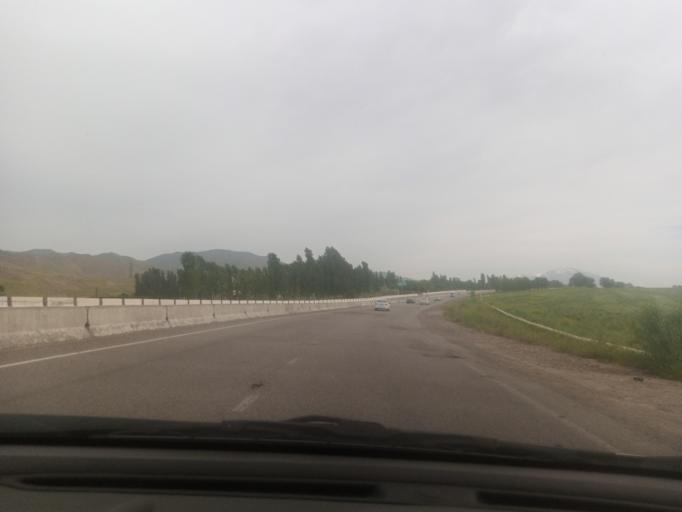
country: UZ
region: Toshkent
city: Angren
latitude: 40.9462
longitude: 69.9077
